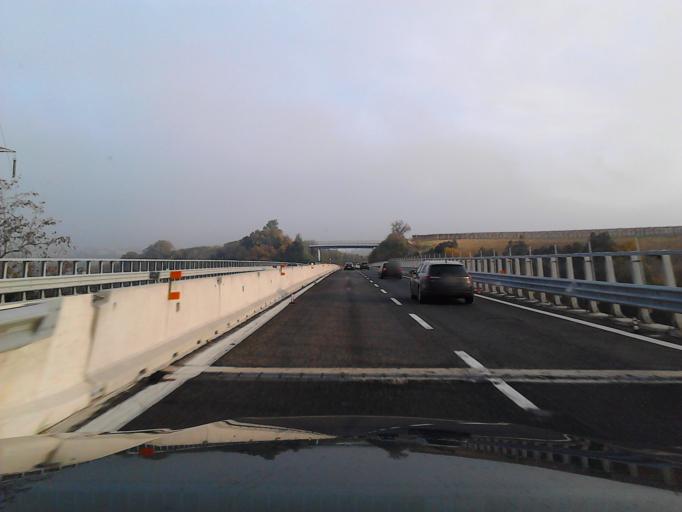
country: IT
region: Abruzzo
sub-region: Provincia di Chieti
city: San Vito Chietino
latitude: 42.3001
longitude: 14.4264
